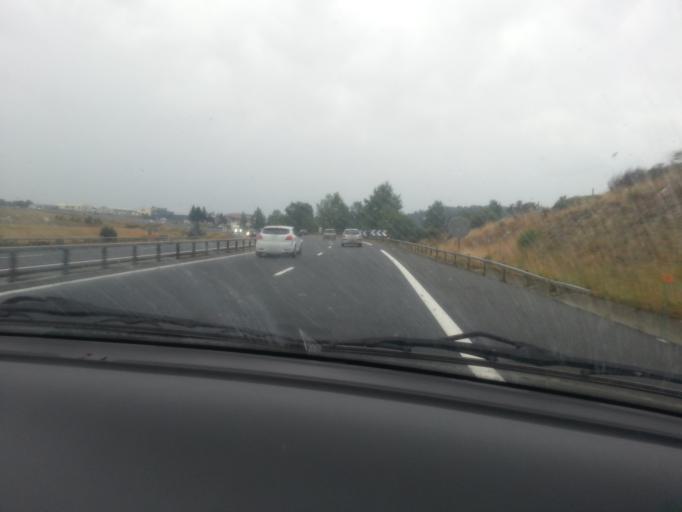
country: FR
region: Languedoc-Roussillon
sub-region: Departement de la Lozere
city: Aumont-Aubrac
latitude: 44.7298
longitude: 3.2885
